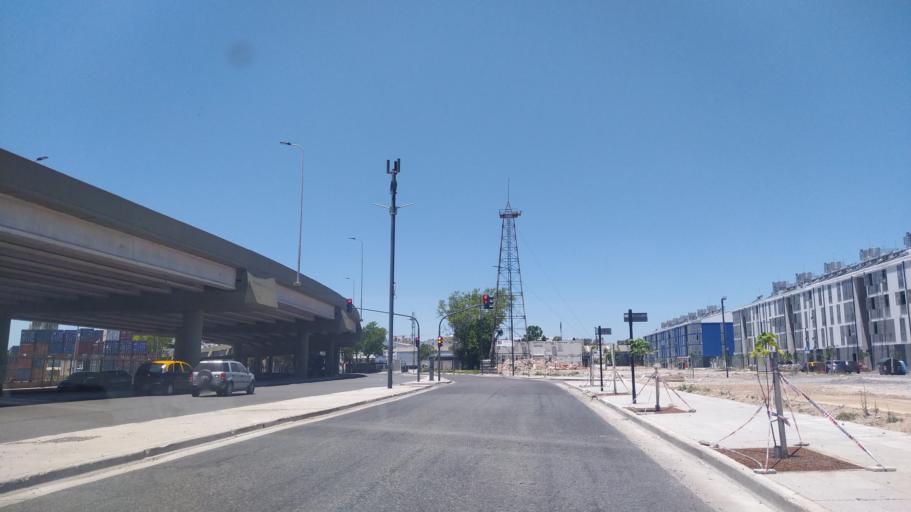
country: AR
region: Buenos Aires F.D.
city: Retiro
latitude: -34.5797
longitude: -58.3815
